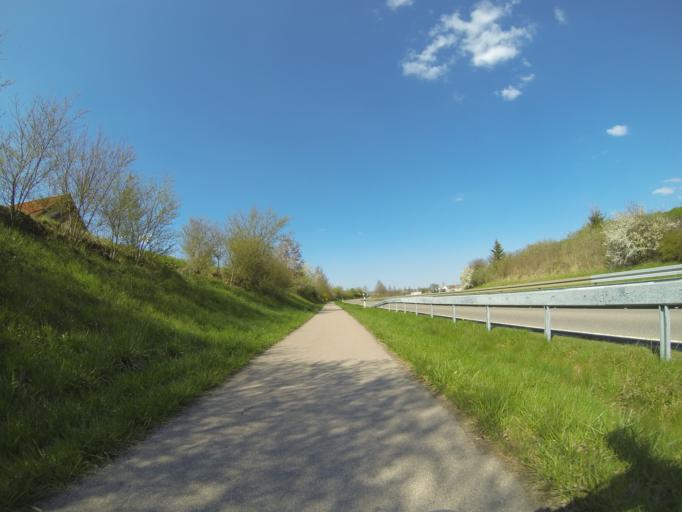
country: DE
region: Baden-Wuerttemberg
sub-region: Tuebingen Region
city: Laupheim
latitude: 48.2253
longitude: 9.9009
